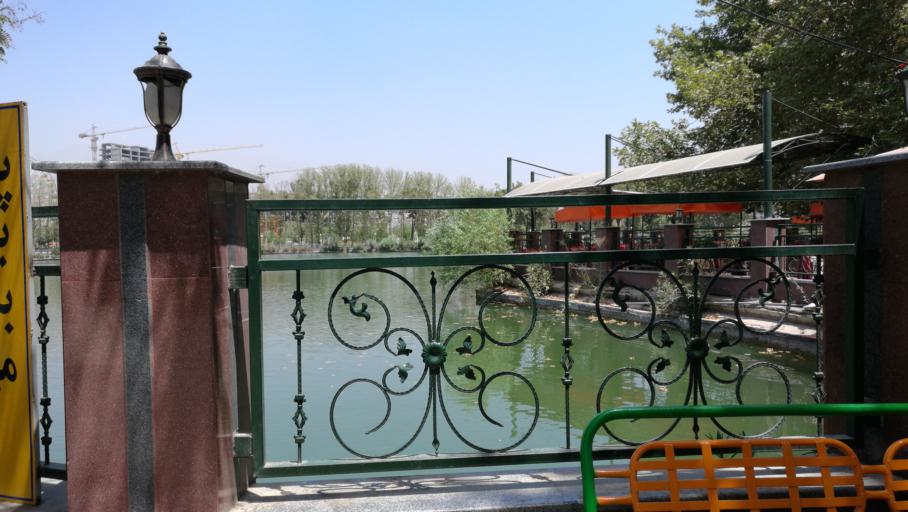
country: IR
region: Tehran
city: Tehran
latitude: 35.7193
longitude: 51.2930
